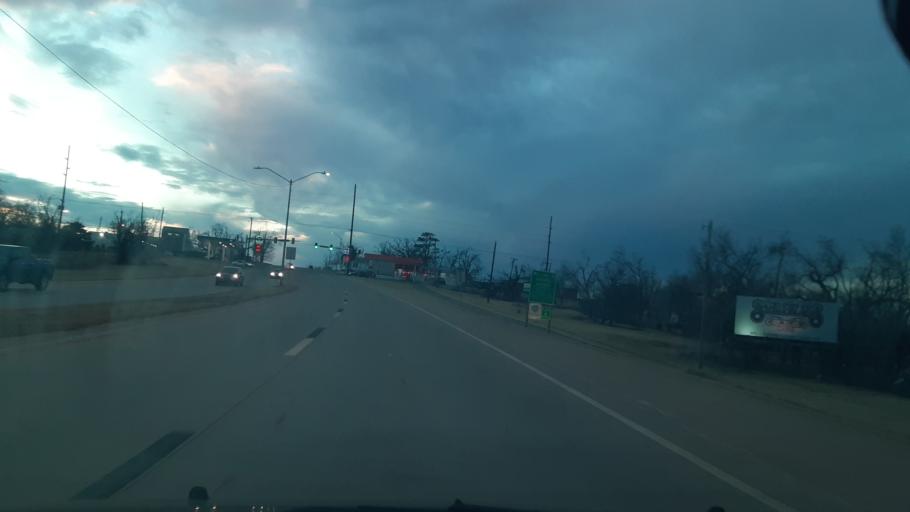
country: US
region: Oklahoma
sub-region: Logan County
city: Guthrie
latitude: 35.8802
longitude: -97.4055
